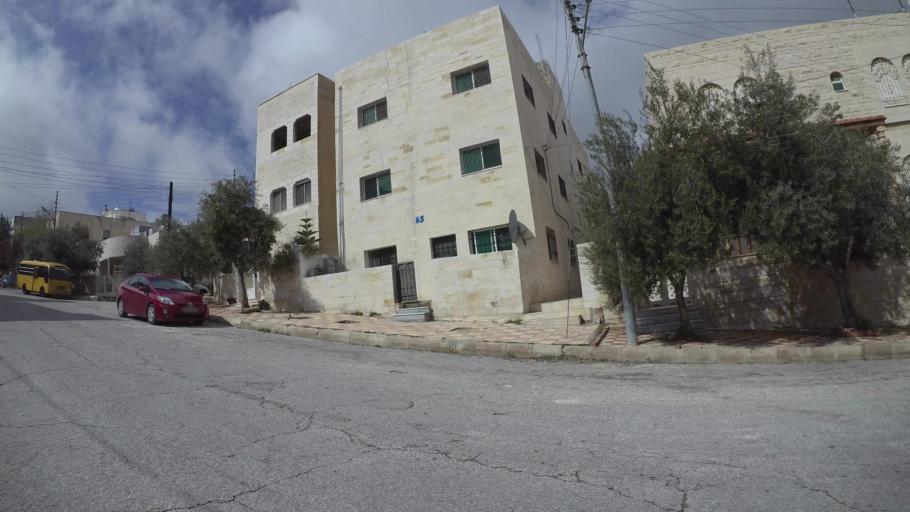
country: JO
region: Amman
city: Al Jubayhah
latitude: 32.0638
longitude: 35.8847
